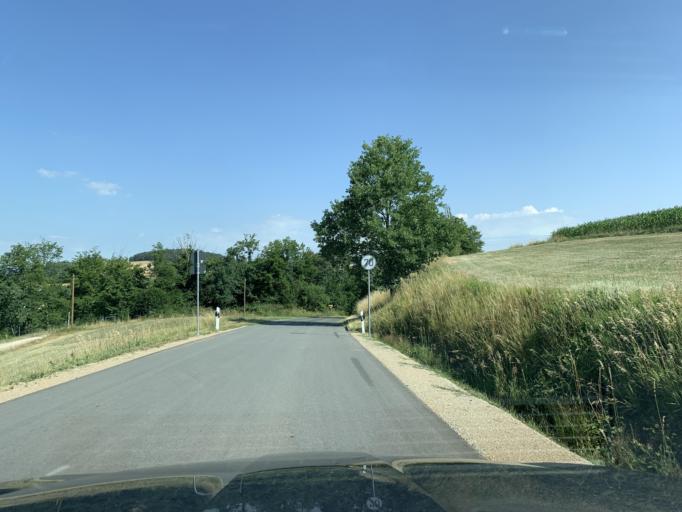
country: DE
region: Bavaria
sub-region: Upper Palatinate
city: Altendorf
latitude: 49.3940
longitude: 12.3109
